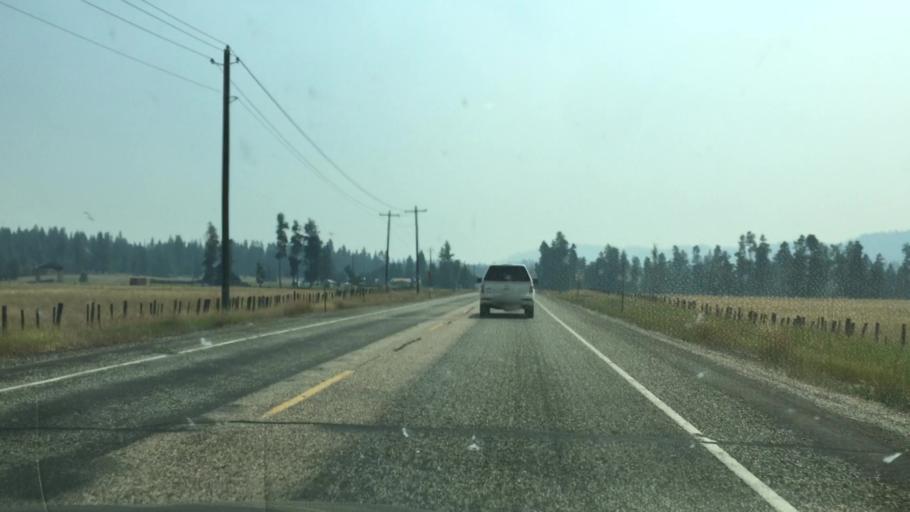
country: US
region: Idaho
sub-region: Valley County
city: Cascade
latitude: 44.3961
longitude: -116.0055
